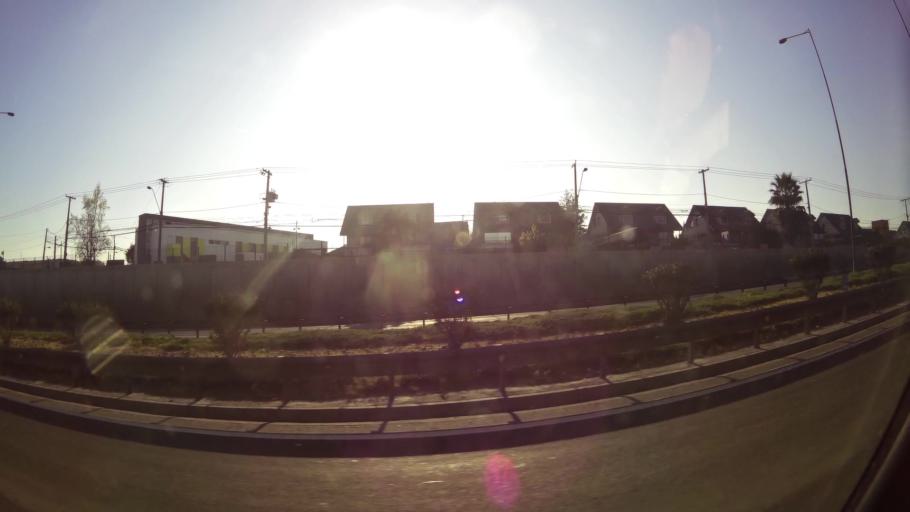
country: CL
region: Santiago Metropolitan
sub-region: Provincia de Santiago
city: Lo Prado
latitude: -33.4645
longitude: -70.7631
